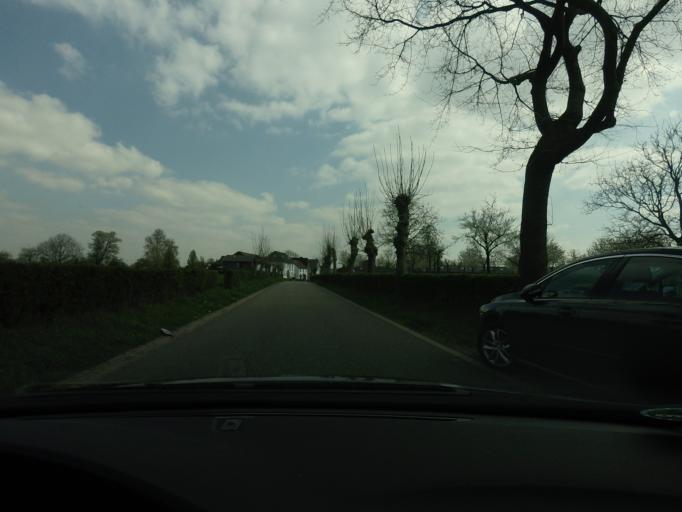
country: NL
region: Limburg
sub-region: Eijsden-Margraten
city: Eijsden
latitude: 50.7851
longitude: 5.7665
